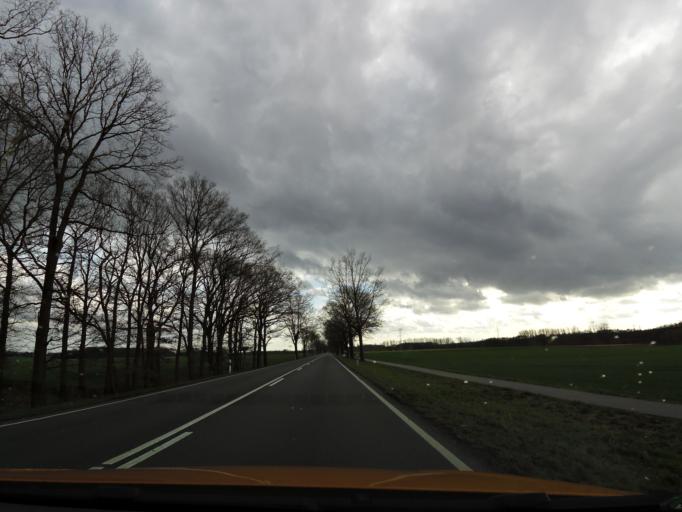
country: DE
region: Lower Saxony
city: Bassum
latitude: 52.8900
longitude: 8.7301
